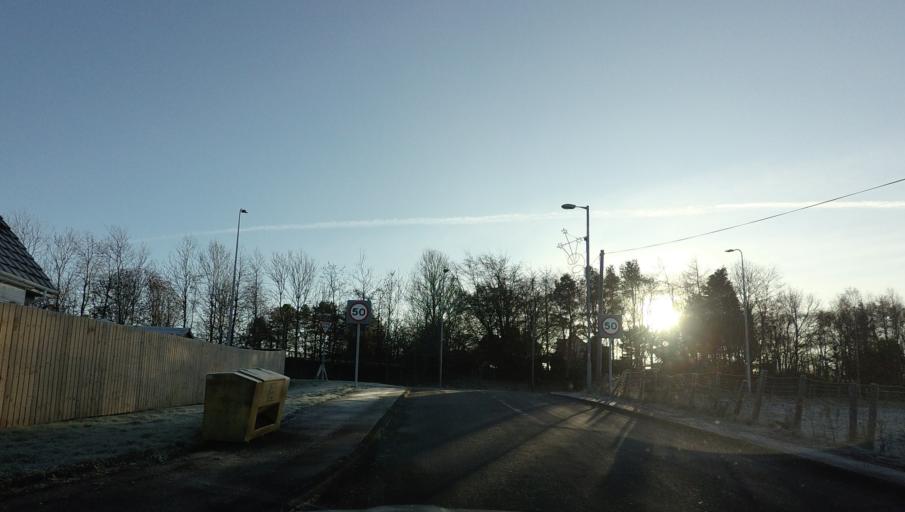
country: GB
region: Scotland
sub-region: North Lanarkshire
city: Newmains
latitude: 55.7912
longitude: -3.8546
